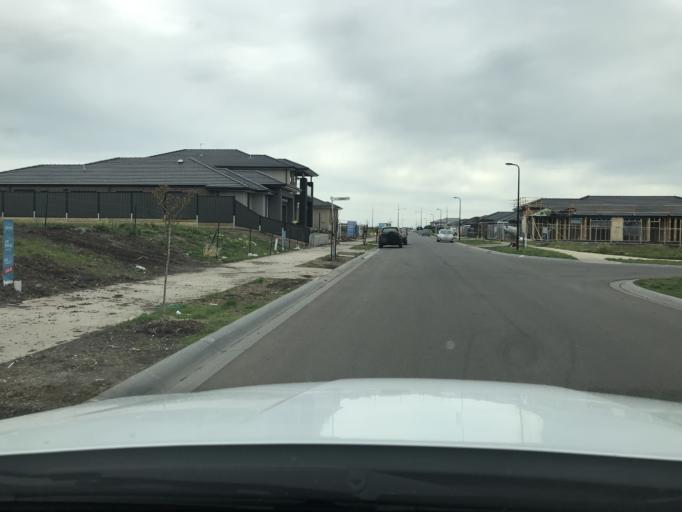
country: AU
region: Victoria
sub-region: Hume
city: Roxburgh Park
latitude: -37.6071
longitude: 144.9093
